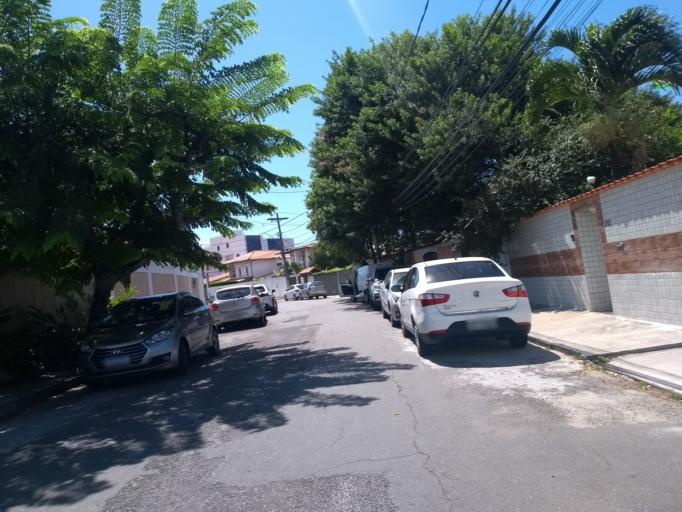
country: BR
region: Bahia
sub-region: Salvador
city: Salvador
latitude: -12.9933
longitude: -38.4600
